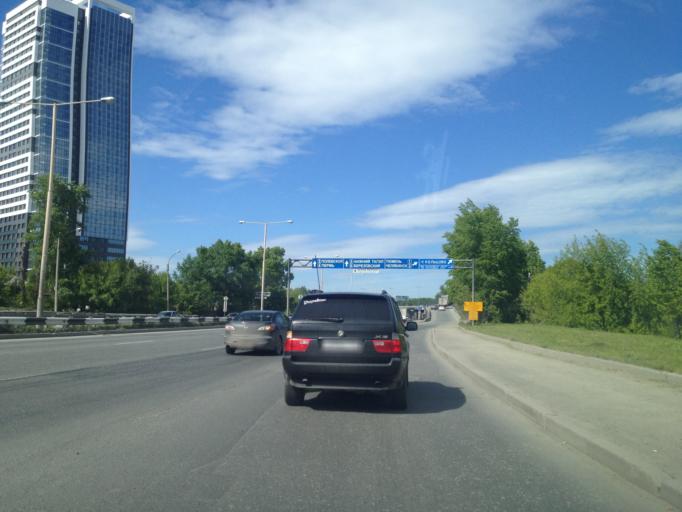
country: RU
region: Sverdlovsk
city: Yekaterinburg
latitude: 56.7961
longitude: 60.6408
